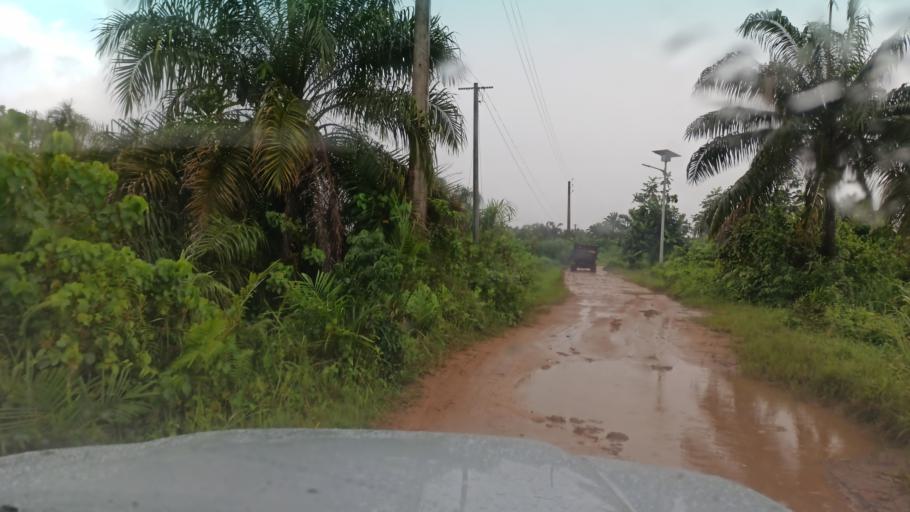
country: BJ
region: Queme
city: Porto-Novo
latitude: 6.4576
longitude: 2.6541
